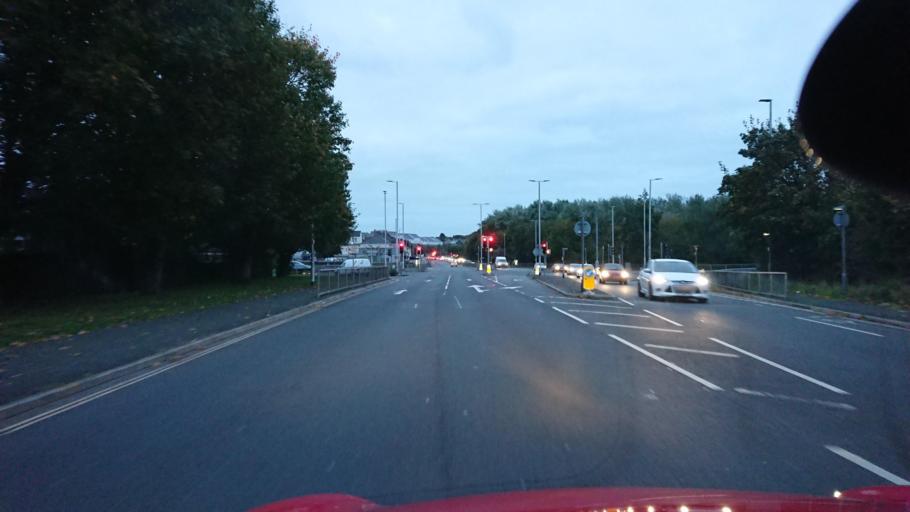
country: GB
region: England
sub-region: Cornwall
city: Torpoint
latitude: 50.3965
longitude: -4.1793
